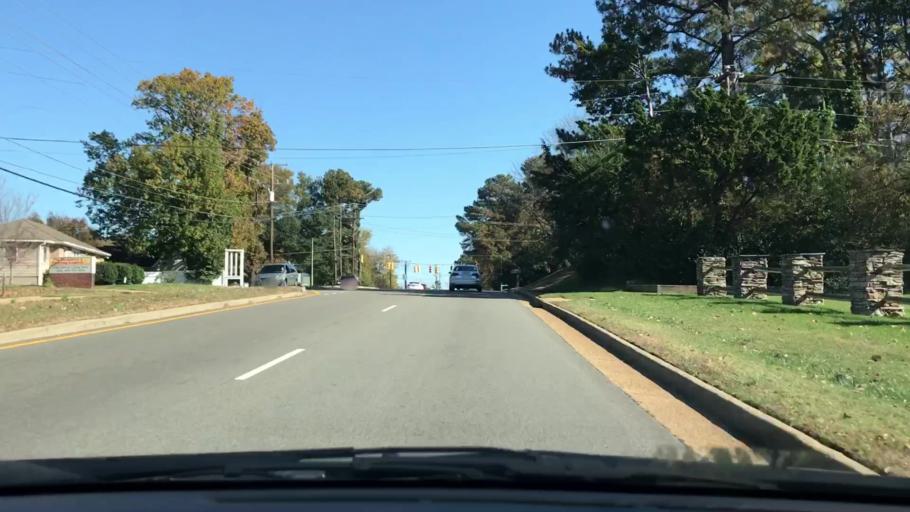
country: US
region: Virginia
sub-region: Henrico County
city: Laurel
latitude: 37.6292
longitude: -77.5406
